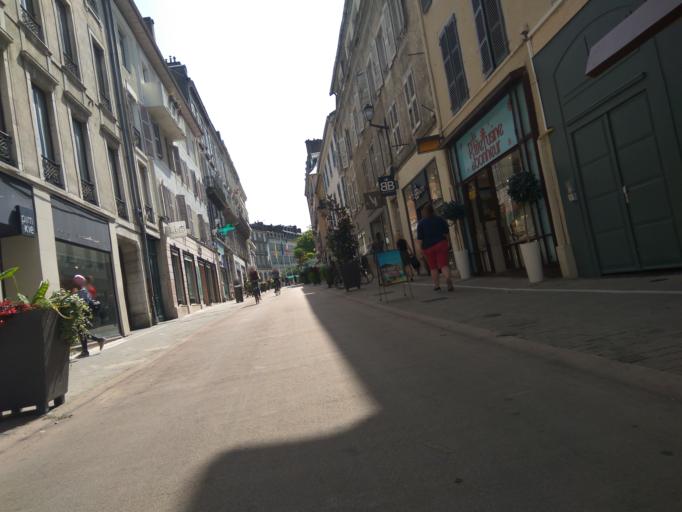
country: FR
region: Aquitaine
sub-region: Departement des Pyrenees-Atlantiques
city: Pau
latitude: 43.2971
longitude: -0.3691
